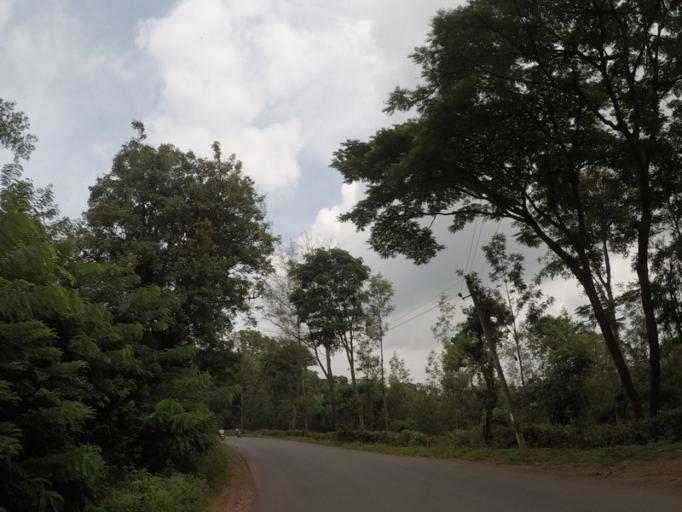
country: IN
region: Karnataka
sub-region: Chikmagalur
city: Chikmagalur
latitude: 13.3680
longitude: 75.7487
